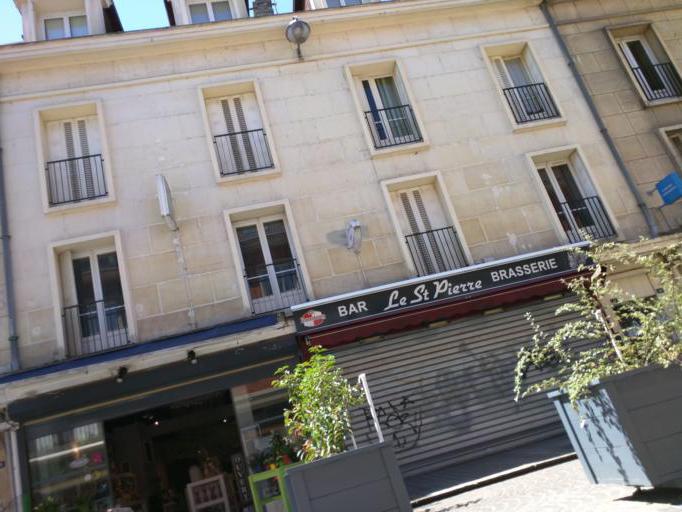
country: FR
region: Picardie
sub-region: Departement de l'Oise
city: Beauvais
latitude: 49.4315
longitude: 2.0829
